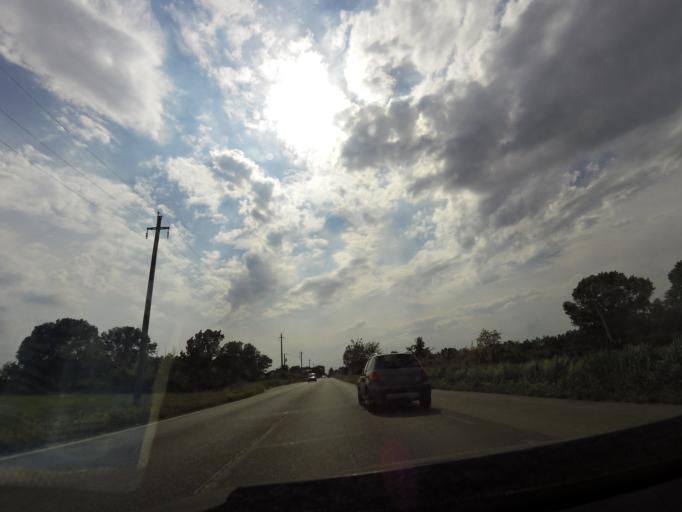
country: IT
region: Lombardy
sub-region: Citta metropolitana di Milano
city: Carpiano
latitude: 45.3505
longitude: 9.2903
